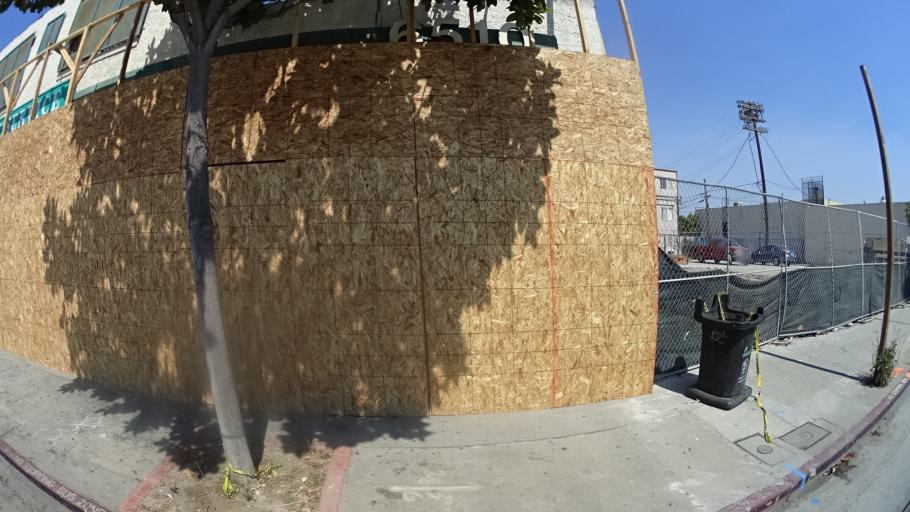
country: US
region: California
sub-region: Los Angeles County
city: View Park-Windsor Hills
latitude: 33.9804
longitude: -118.3307
